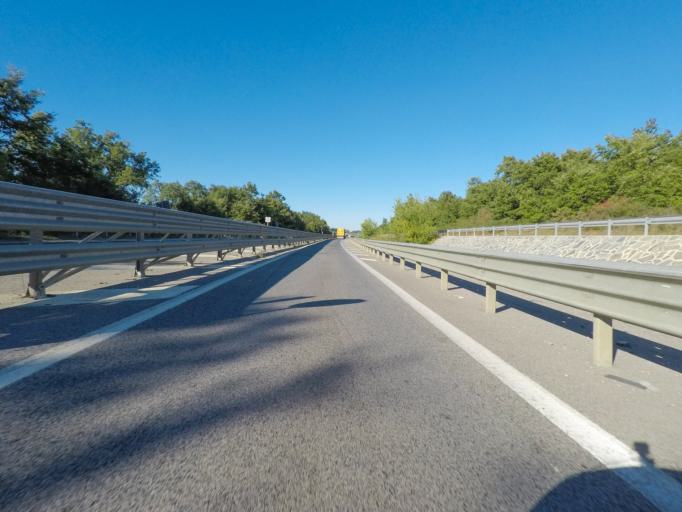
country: IT
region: Tuscany
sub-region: Provincia di Siena
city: Rosia
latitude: 43.2233
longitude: 11.2737
